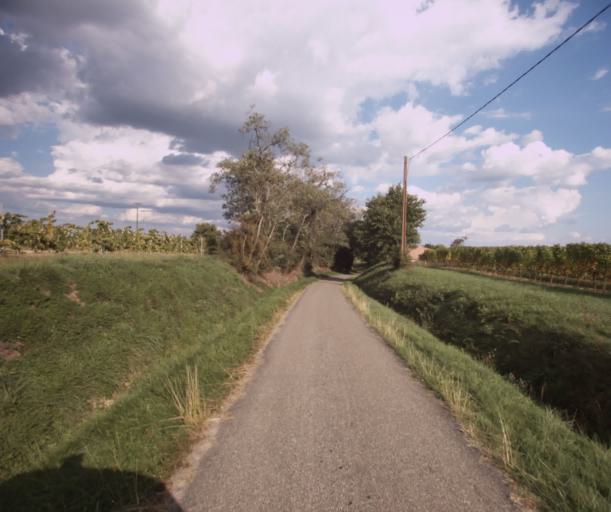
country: FR
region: Midi-Pyrenees
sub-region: Departement du Gers
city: Cazaubon
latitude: 43.8801
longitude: -0.0636
